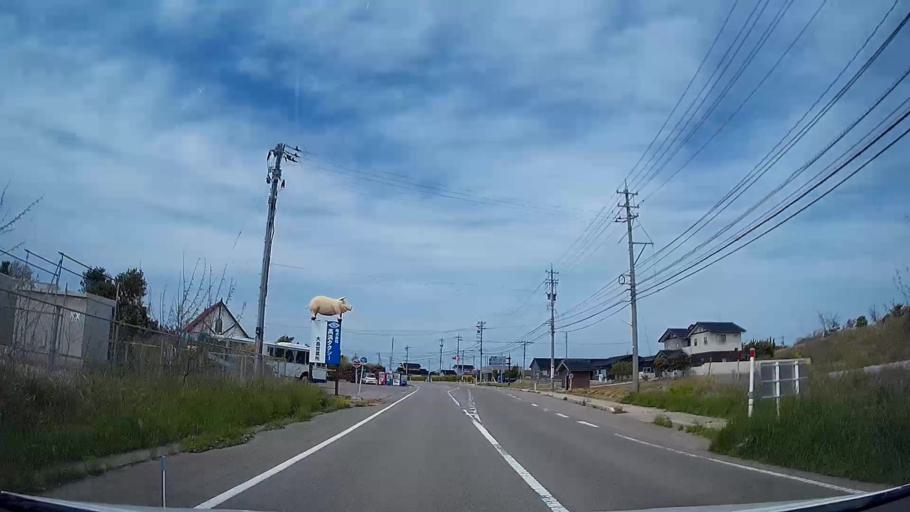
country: JP
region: Ishikawa
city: Hakui
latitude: 36.9776
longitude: 136.7763
